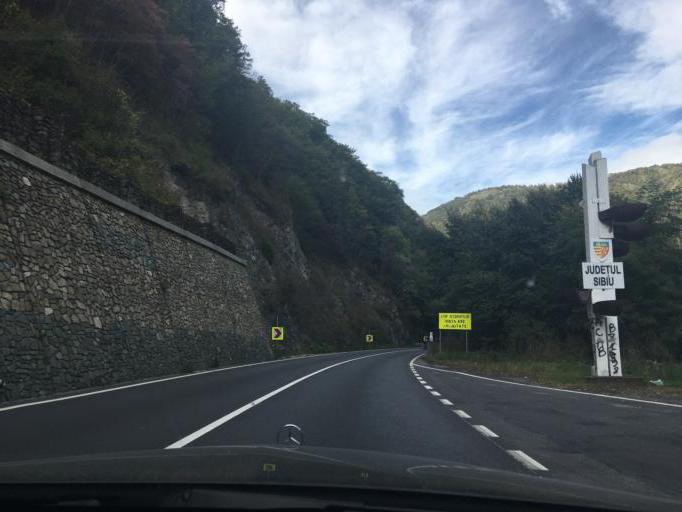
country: RO
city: Cainenii Mici
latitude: 45.5536
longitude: 24.2644
